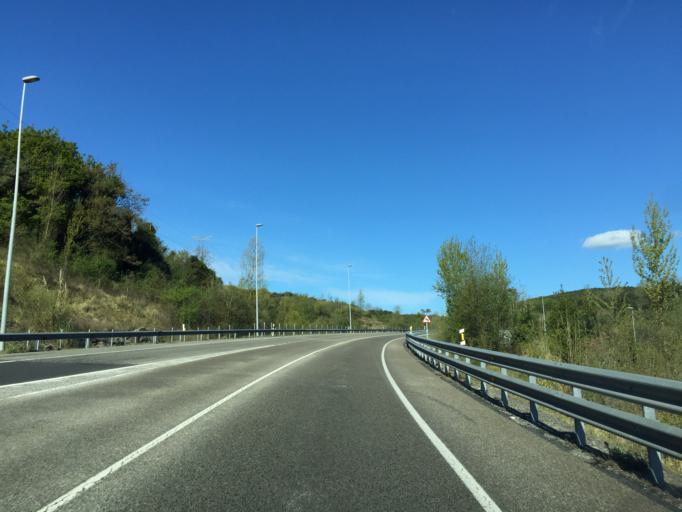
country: ES
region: Asturias
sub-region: Province of Asturias
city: Llanera
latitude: 43.3643
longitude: -5.9520
